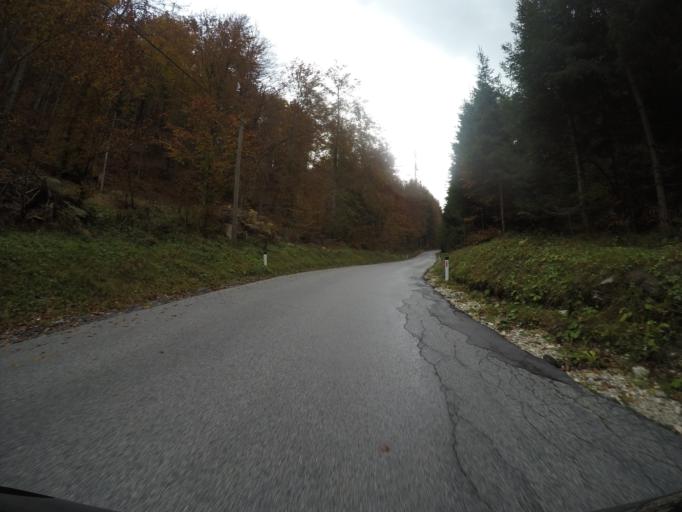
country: SI
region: Kranjska Gora
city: Mojstrana
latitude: 46.4408
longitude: 13.9319
